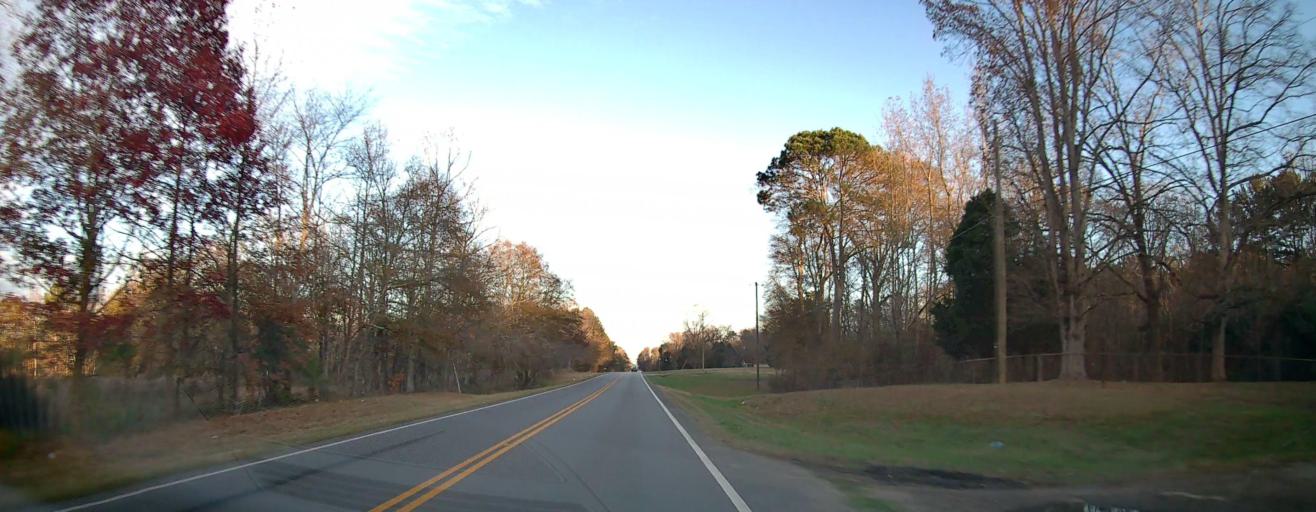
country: US
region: Alabama
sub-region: Saint Clair County
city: Steele
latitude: 34.0538
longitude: -86.1992
